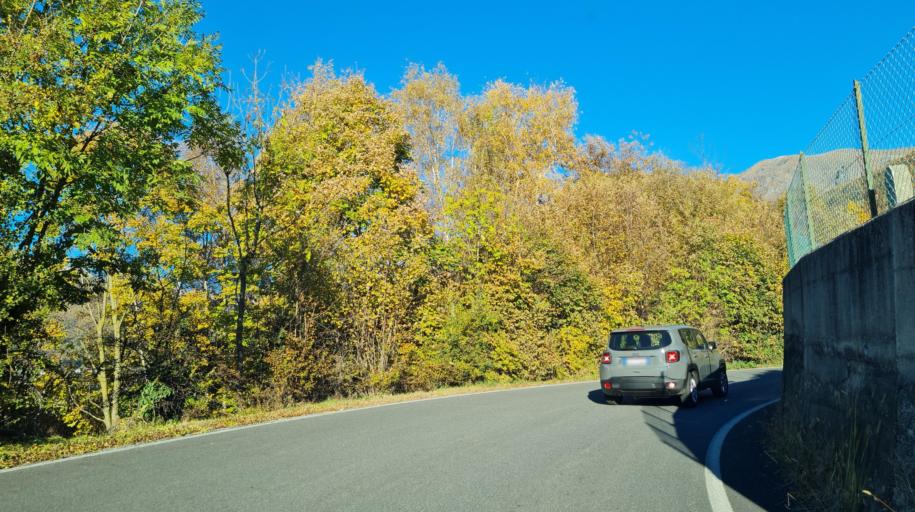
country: IT
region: Piedmont
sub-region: Provincia di Torino
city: Trausella
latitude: 45.4952
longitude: 7.7677
